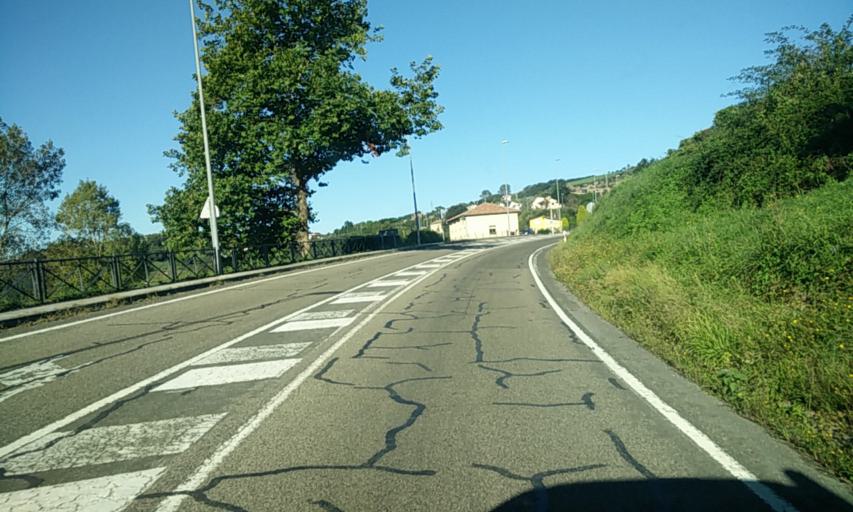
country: ES
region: Cantabria
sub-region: Provincia de Cantabria
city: San Vicente de la Barquera
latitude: 43.3874
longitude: -4.4008
